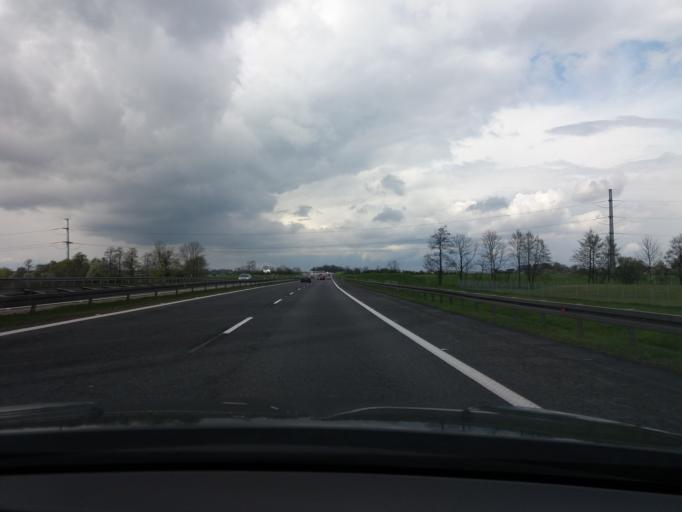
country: PL
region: Lower Silesian Voivodeship
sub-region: Powiat wroclawski
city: Zorawina
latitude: 51.0091
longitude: 17.0297
